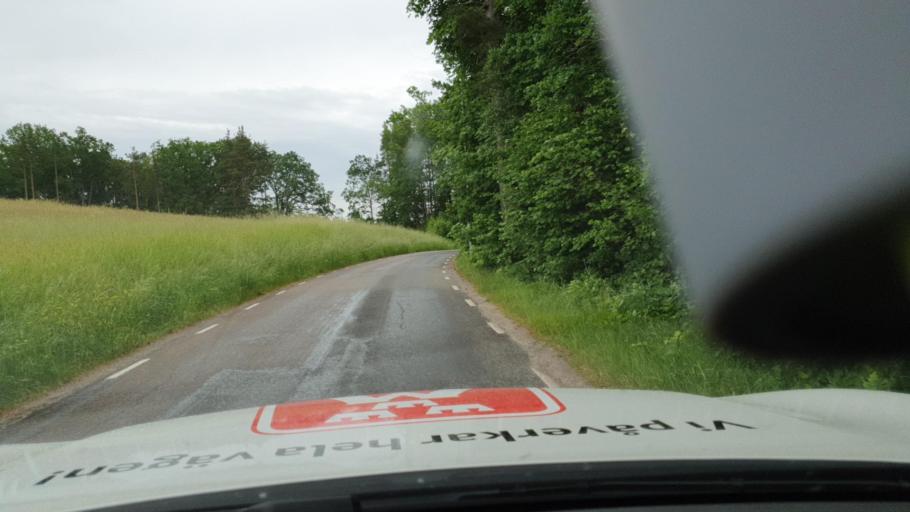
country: SE
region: Vaestra Goetaland
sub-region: Hjo Kommun
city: Hjo
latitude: 58.3136
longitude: 14.2554
